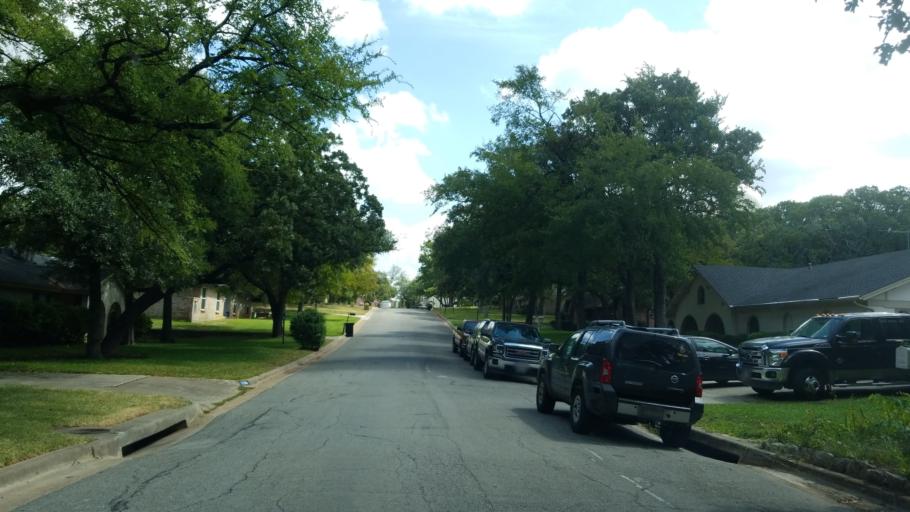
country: US
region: Texas
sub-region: Tarrant County
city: Euless
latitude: 32.8575
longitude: -97.0844
